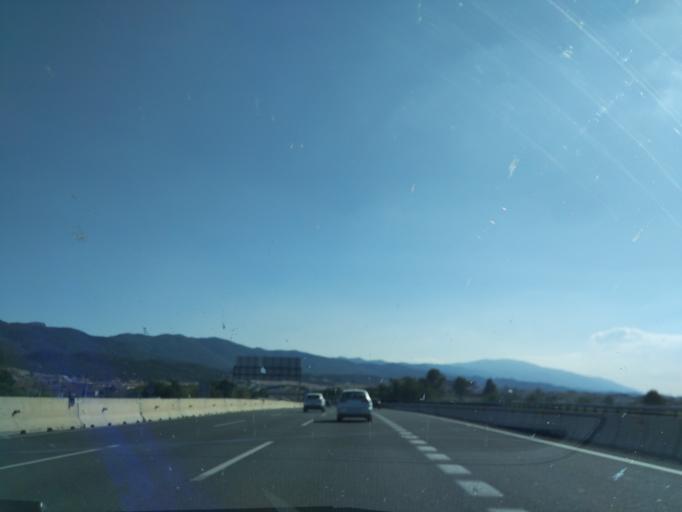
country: ES
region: Murcia
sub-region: Murcia
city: Murcia
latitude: 37.9472
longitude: -1.1468
